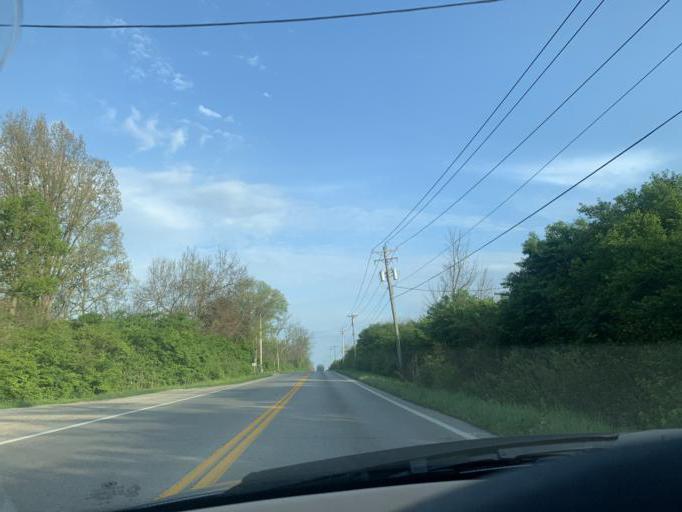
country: US
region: Ohio
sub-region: Hamilton County
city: Glendale
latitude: 39.2706
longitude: -84.4750
